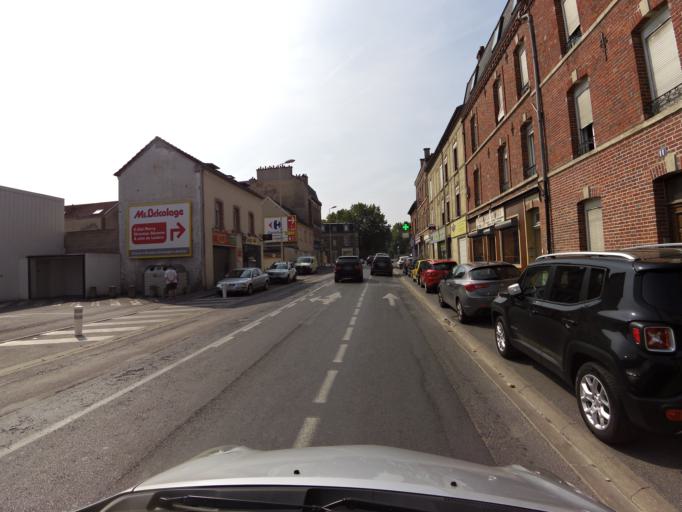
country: FR
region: Champagne-Ardenne
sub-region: Departement de la Marne
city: Magenta
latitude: 49.0475
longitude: 3.9649
